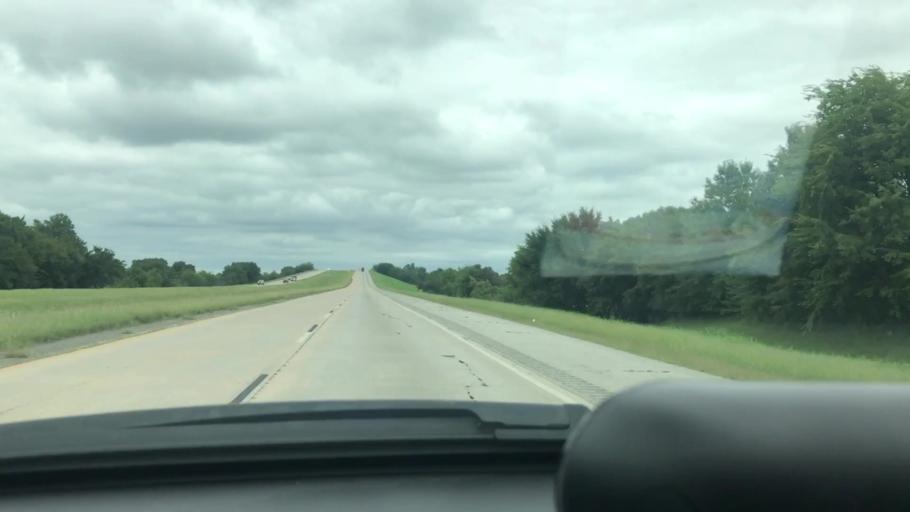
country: US
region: Oklahoma
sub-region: Wagoner County
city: Wagoner
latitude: 35.8775
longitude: -95.4026
